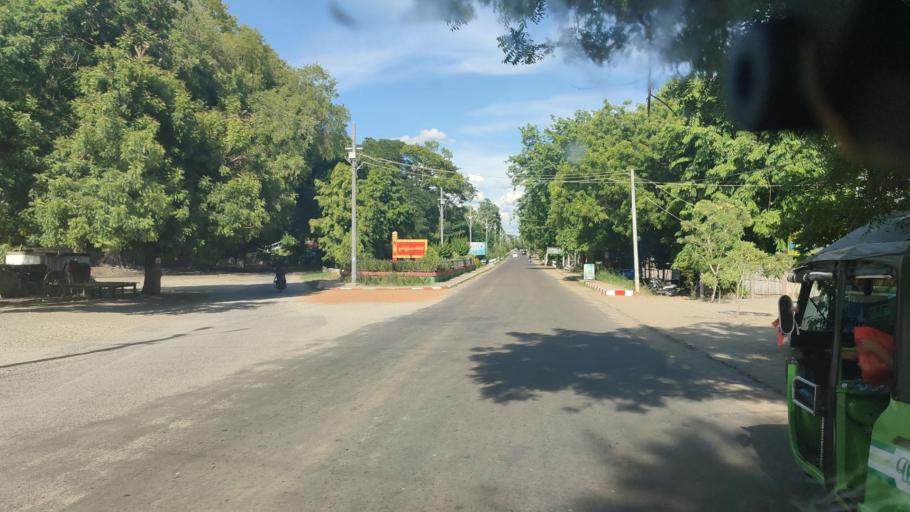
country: MM
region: Magway
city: Chauk
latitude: 20.9045
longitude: 94.7935
